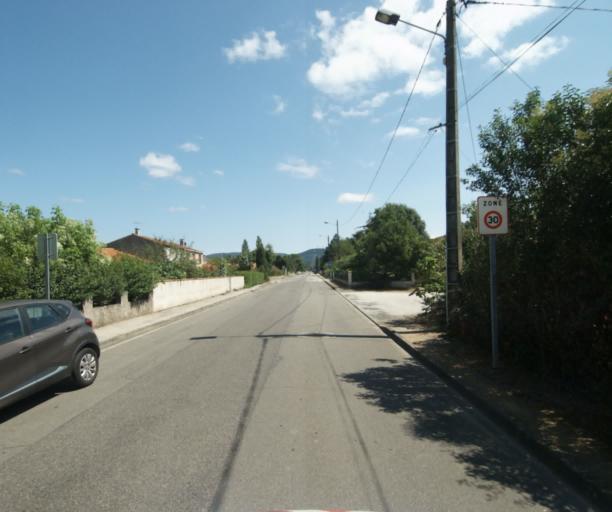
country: FR
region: Midi-Pyrenees
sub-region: Departement de la Haute-Garonne
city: Revel
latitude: 43.4629
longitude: 2.0088
